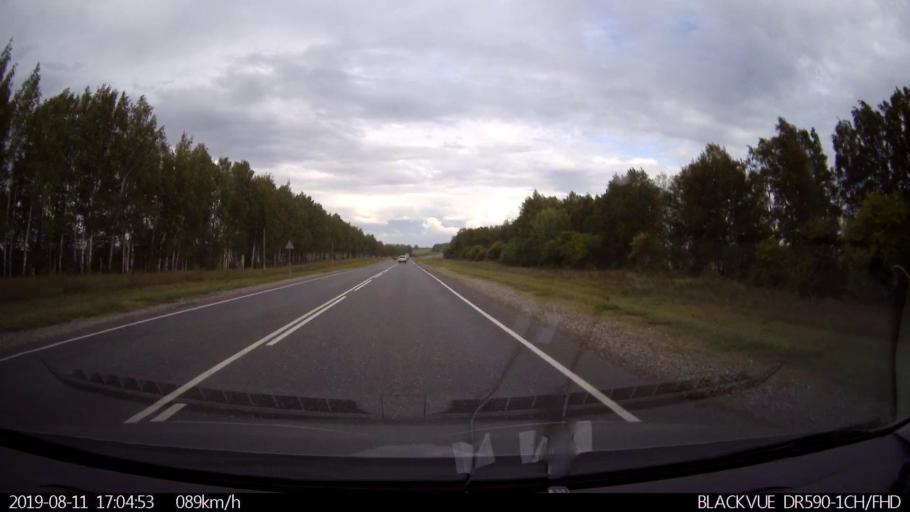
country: RU
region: Ulyanovsk
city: Mayna
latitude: 54.2998
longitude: 47.7731
